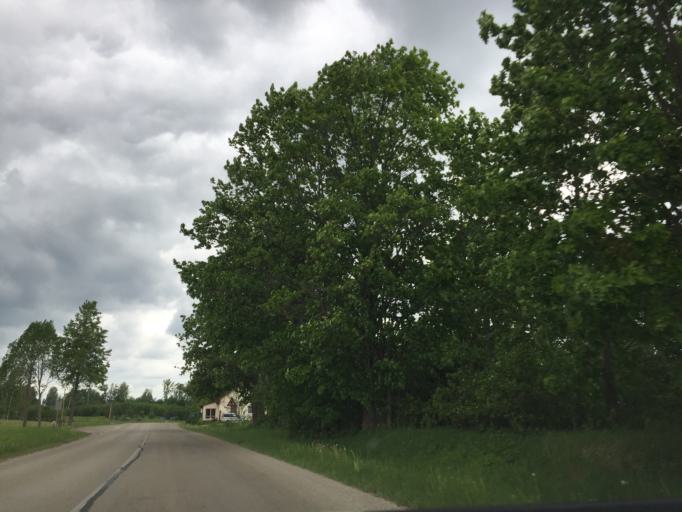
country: LV
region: Dagda
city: Dagda
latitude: 56.1170
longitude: 27.4760
